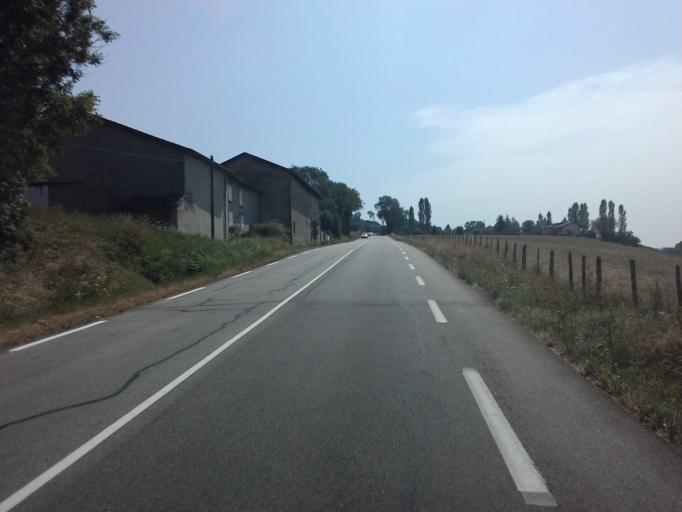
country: FR
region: Rhone-Alpes
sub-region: Departement de l'Isere
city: Montferrat
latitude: 45.4782
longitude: 5.5885
